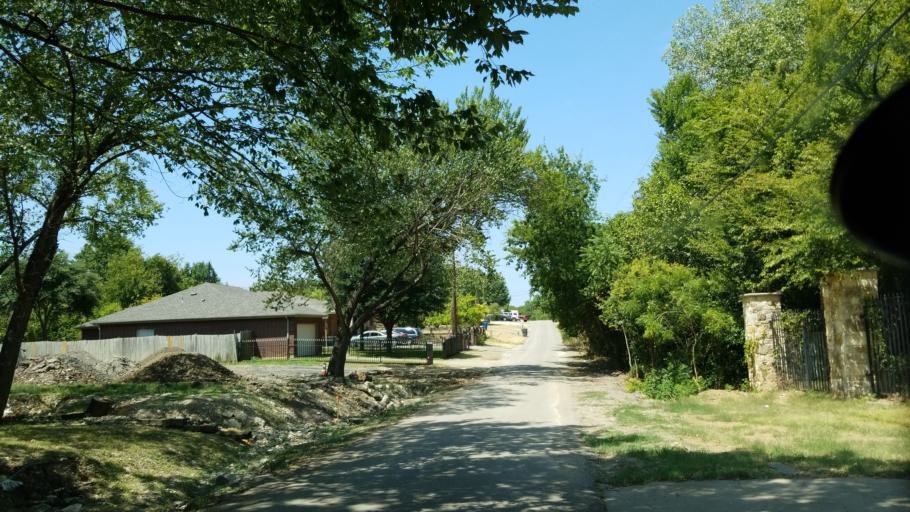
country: US
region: Texas
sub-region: Dallas County
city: Cockrell Hill
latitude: 32.7328
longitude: -96.8950
